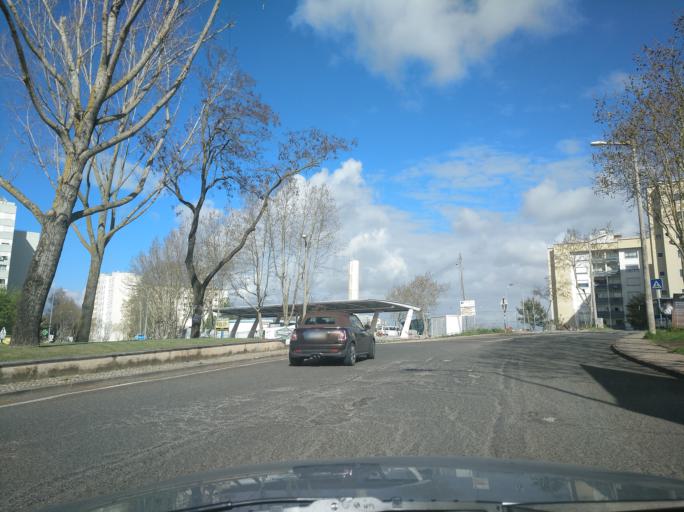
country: PT
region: Lisbon
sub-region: Odivelas
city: Povoa de Santo Adriao
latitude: 38.8134
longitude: -9.1668
